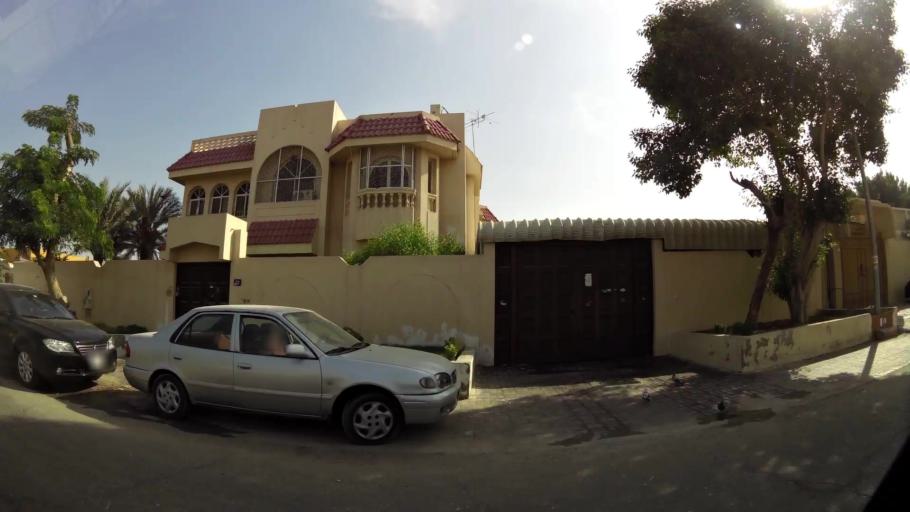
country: AE
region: Ash Shariqah
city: Sharjah
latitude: 25.2243
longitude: 55.3962
